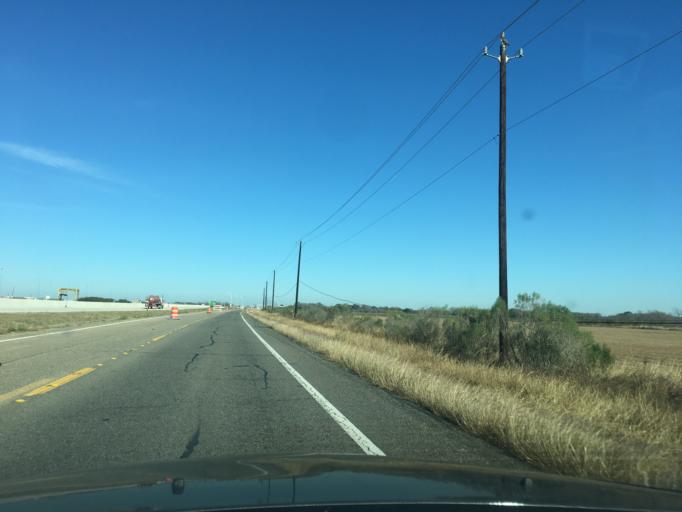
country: US
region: Texas
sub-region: Wharton County
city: East Bernard
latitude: 29.4598
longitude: -95.9778
